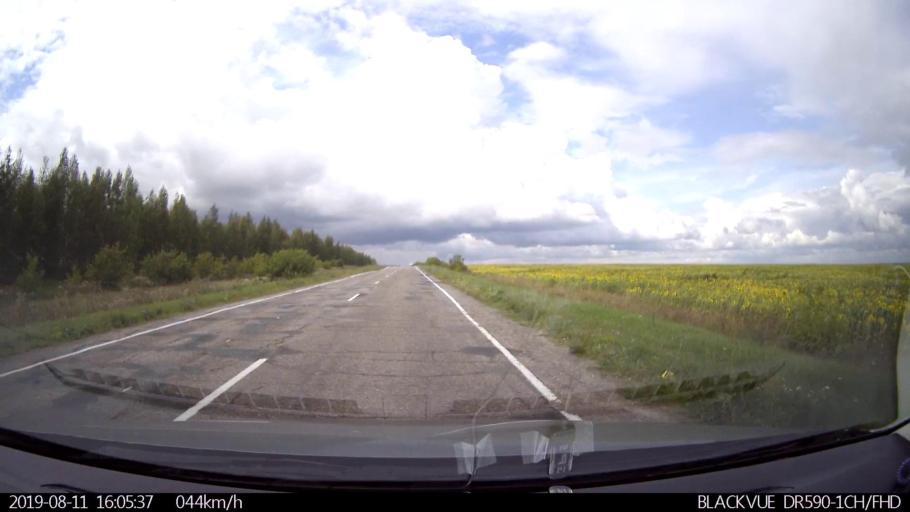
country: RU
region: Ulyanovsk
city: Ignatovka
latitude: 53.9619
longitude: 47.6491
